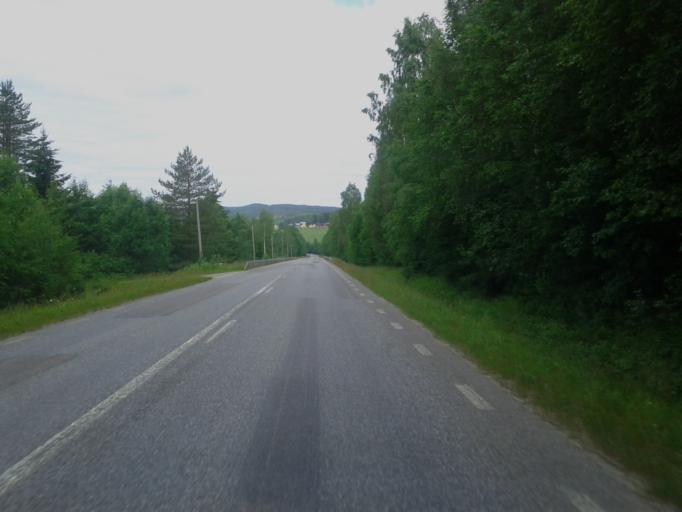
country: SE
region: Vaesternorrland
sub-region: OErnskoeldsviks Kommun
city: Bjasta
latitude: 63.2366
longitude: 18.4426
